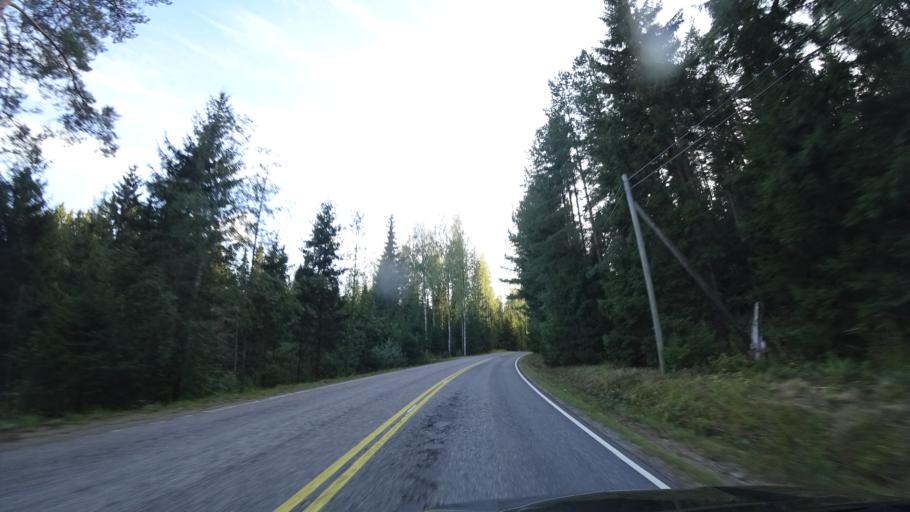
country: FI
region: Haeme
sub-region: Haemeenlinna
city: Lammi
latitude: 61.0149
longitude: 24.9032
